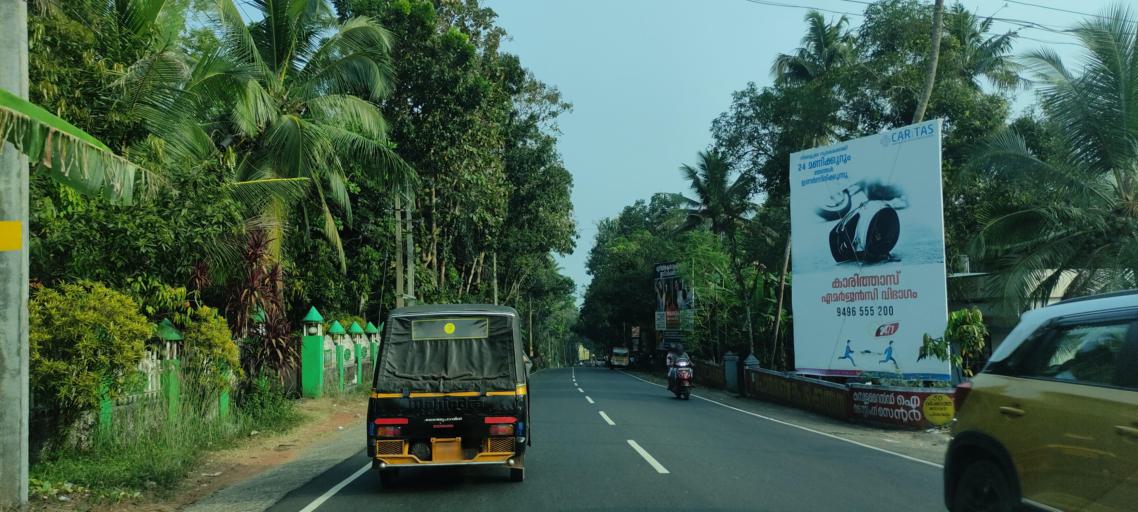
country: IN
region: Kerala
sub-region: Kottayam
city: Vaikam
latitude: 9.7594
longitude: 76.4939
